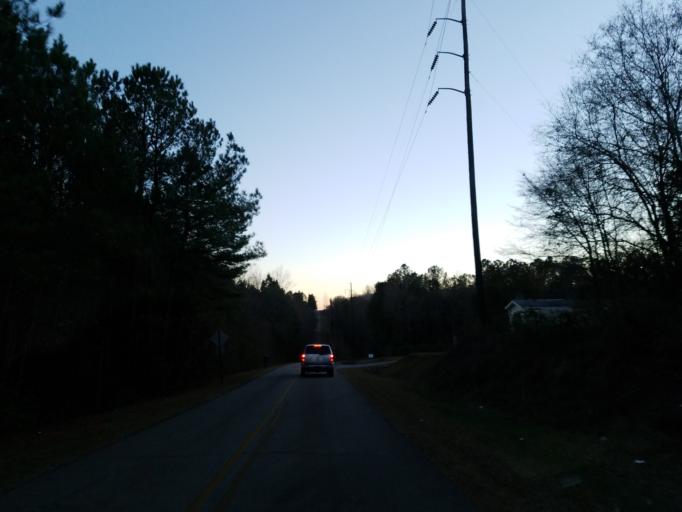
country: US
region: Georgia
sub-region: Monroe County
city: Forsyth
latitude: 33.0100
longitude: -83.8787
